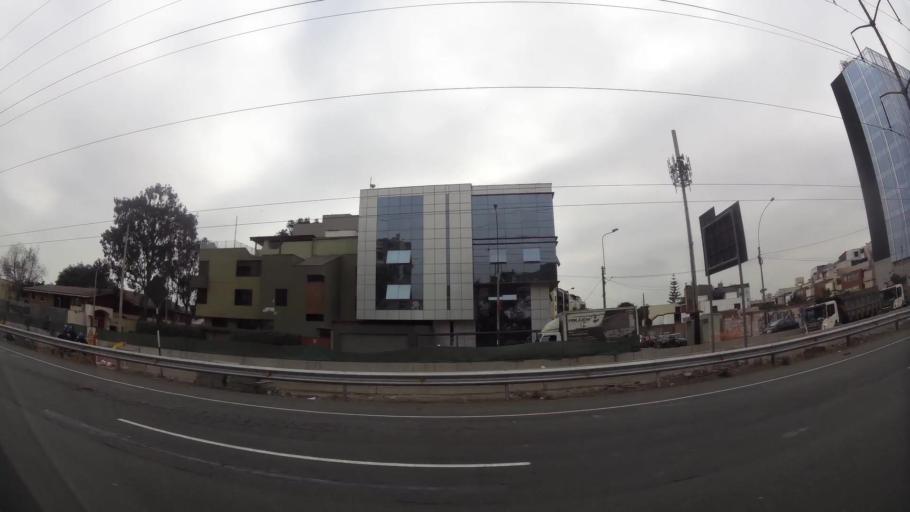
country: PE
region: Lima
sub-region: Lima
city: Surco
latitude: -12.1256
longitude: -76.9771
